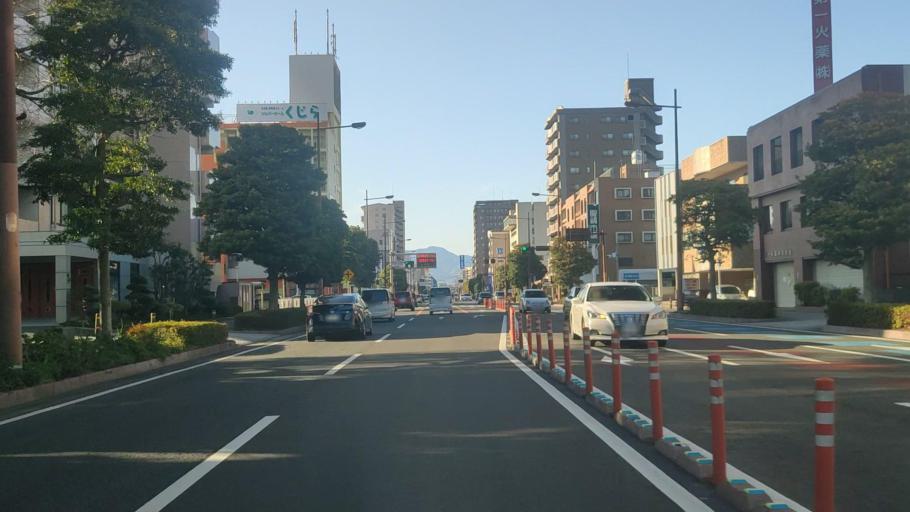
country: JP
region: Oita
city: Oita
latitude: 33.2397
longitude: 131.5964
